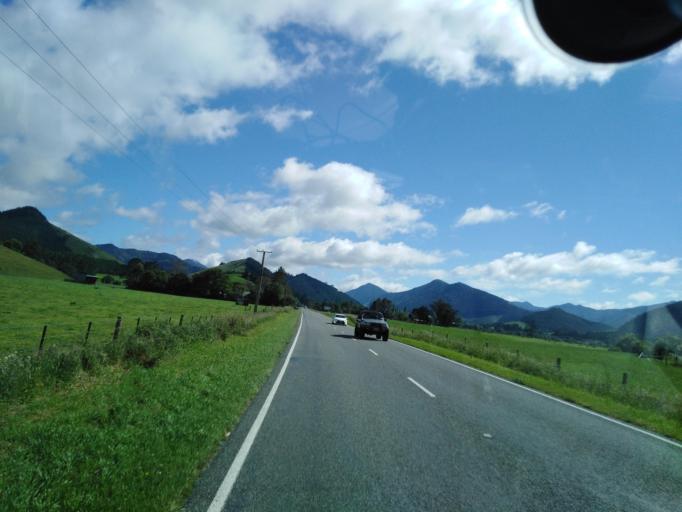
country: NZ
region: Nelson
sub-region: Nelson City
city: Nelson
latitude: -41.2426
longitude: 173.5781
